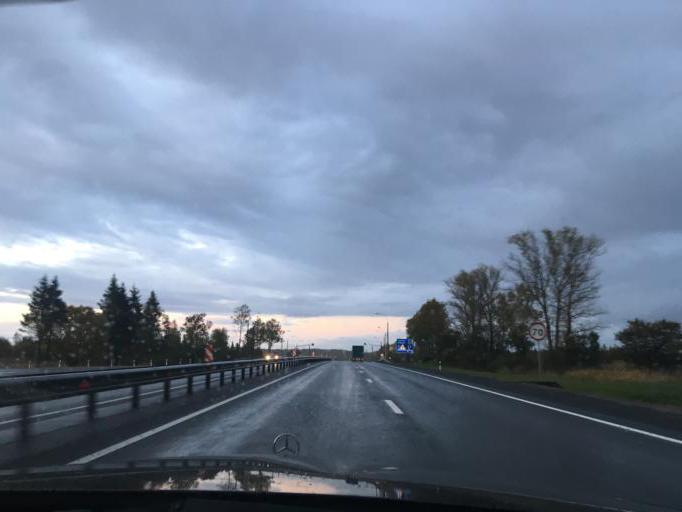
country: RU
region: Smolensk
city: Verkhnedneprovskiy
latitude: 55.1798
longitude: 33.4578
